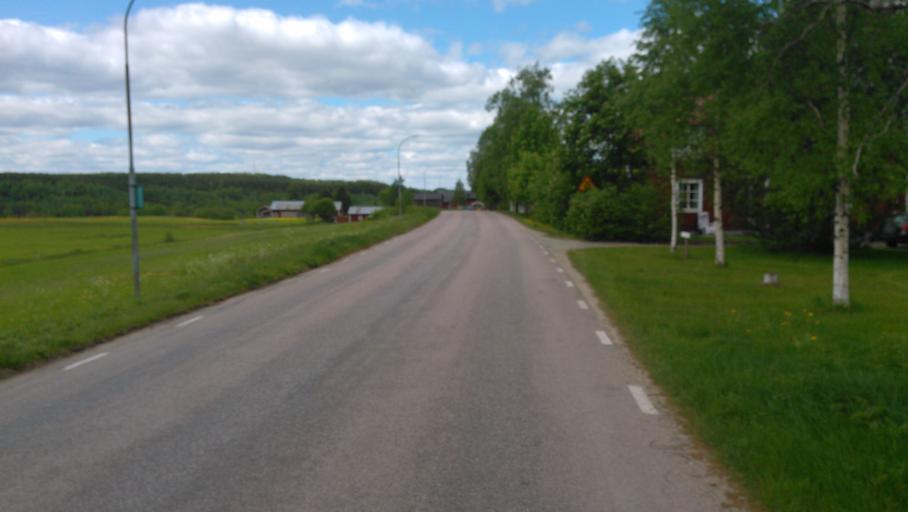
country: SE
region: Vaesterbotten
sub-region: Umea Kommun
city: Roback
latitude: 63.8647
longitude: 20.0815
